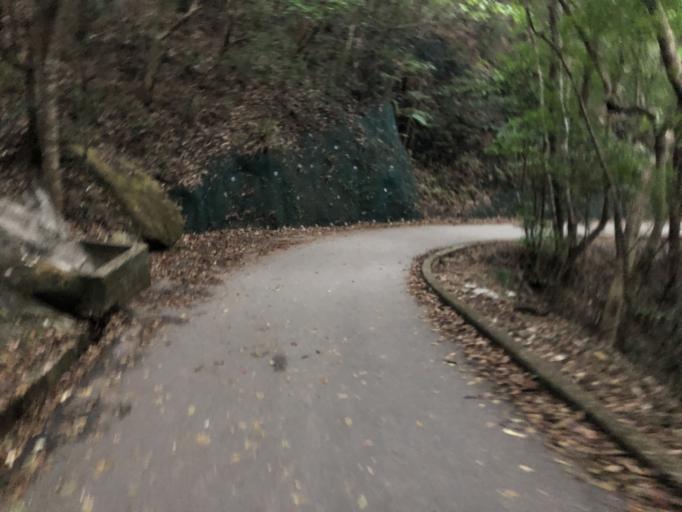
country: HK
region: Wanchai
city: Wan Chai
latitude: 22.2616
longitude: 114.2141
